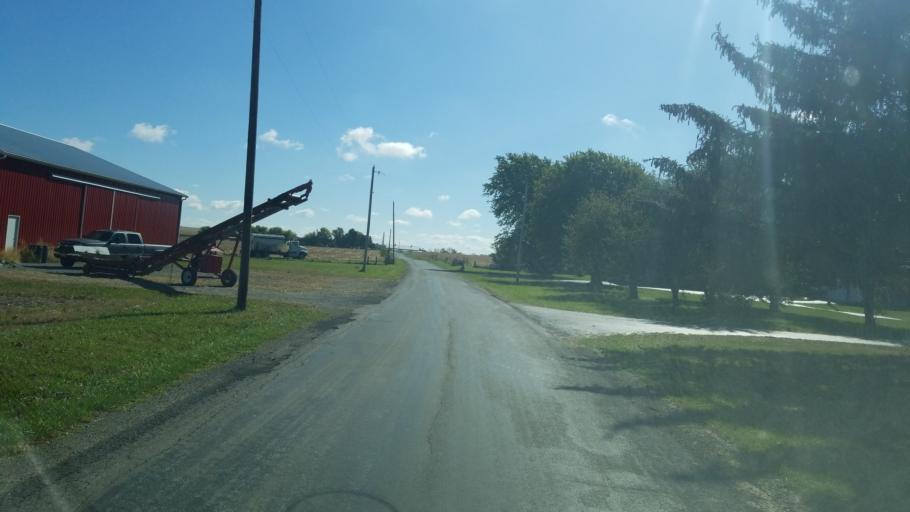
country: US
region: Ohio
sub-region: Highland County
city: Leesburg
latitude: 39.2799
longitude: -83.5718
